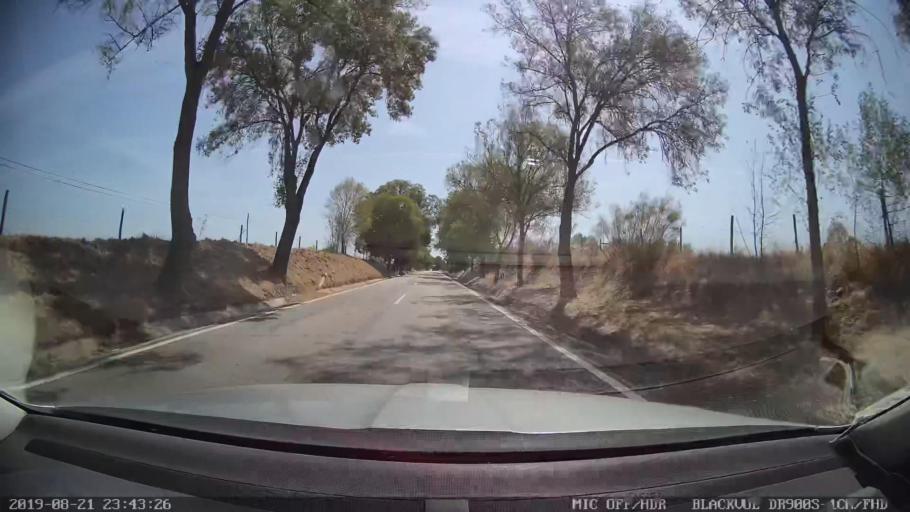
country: PT
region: Castelo Branco
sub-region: Idanha-A-Nova
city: Idanha-a-Nova
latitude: 39.8498
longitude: -7.2944
